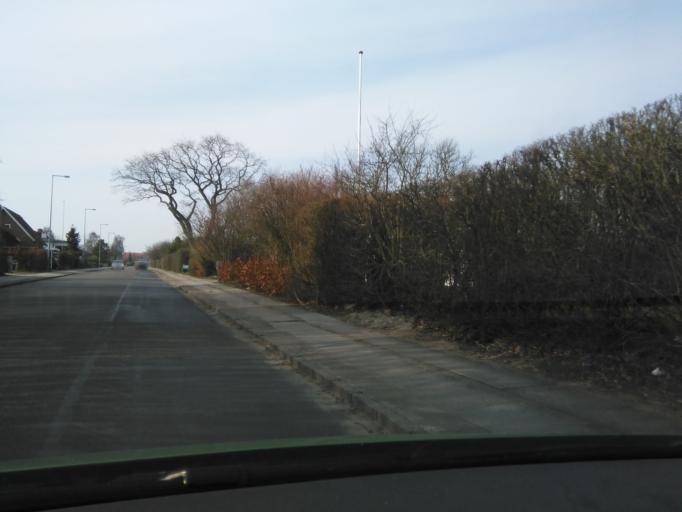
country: DK
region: Central Jutland
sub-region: Arhus Kommune
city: Arhus
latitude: 56.1923
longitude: 10.2272
